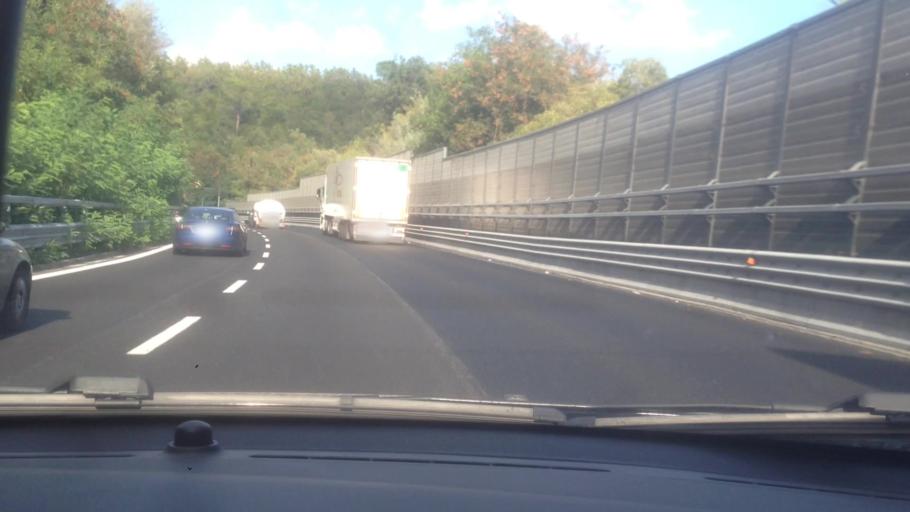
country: IT
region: Liguria
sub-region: Provincia di Genova
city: Cogoleto
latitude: 44.3923
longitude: 8.6537
